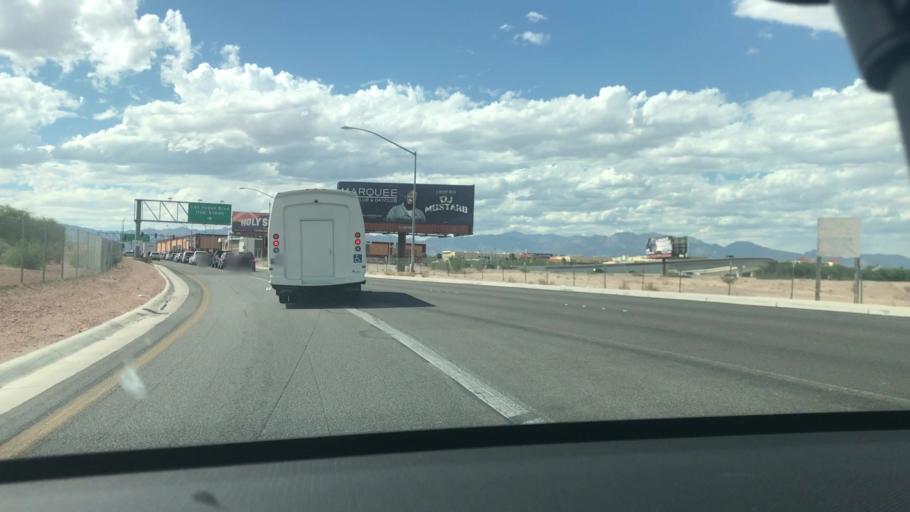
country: US
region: Nevada
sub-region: Clark County
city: Paradise
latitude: 36.0644
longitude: -115.1695
